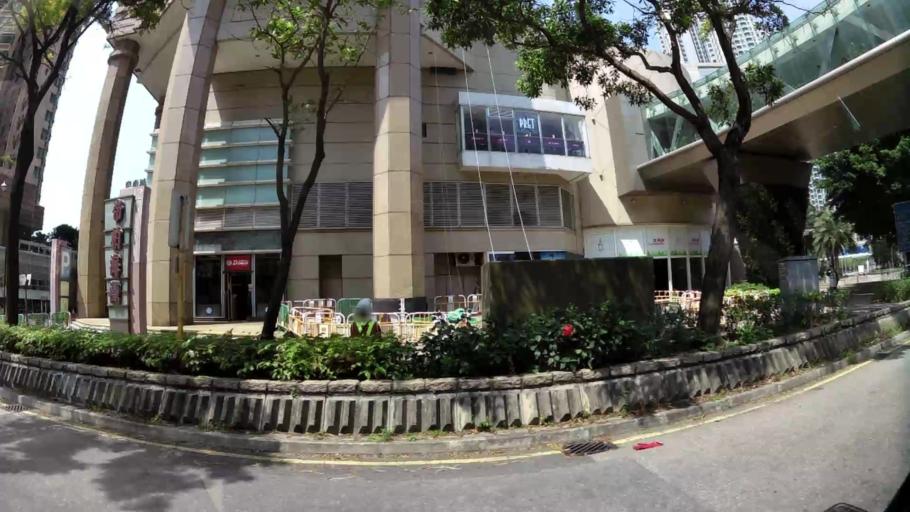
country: HK
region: Sham Shui Po
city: Sham Shui Po
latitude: 22.3174
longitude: 114.1634
